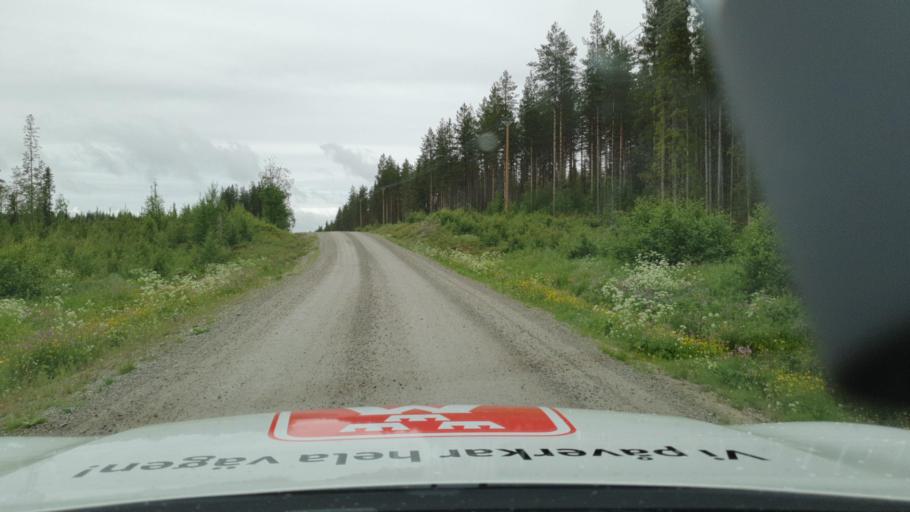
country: SE
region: Vaesterbotten
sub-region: Asele Kommun
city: Asele
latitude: 63.9699
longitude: 17.0692
